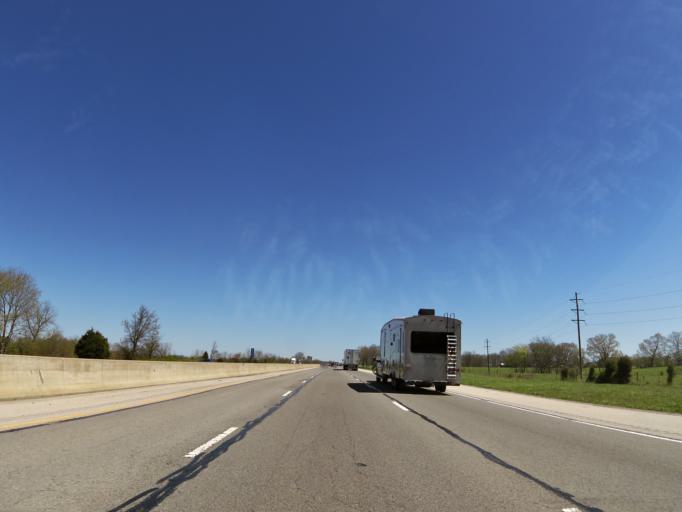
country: US
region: Kentucky
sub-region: Warren County
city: Bowling Green
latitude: 37.0104
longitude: -86.3460
